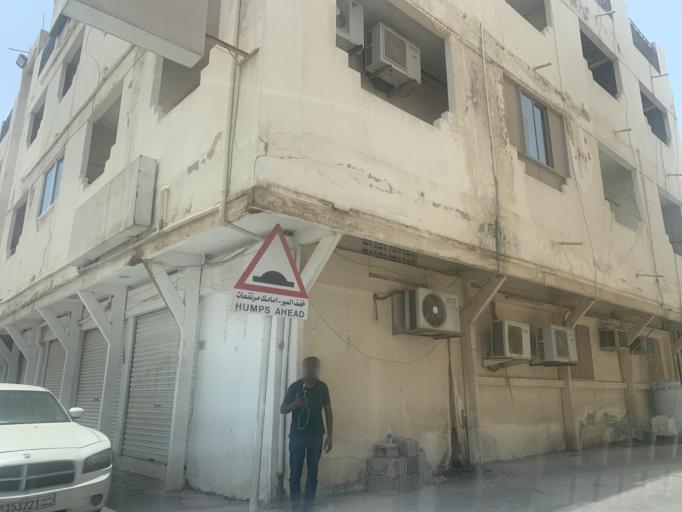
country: BH
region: Manama
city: Jidd Hafs
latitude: 26.2157
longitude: 50.4613
